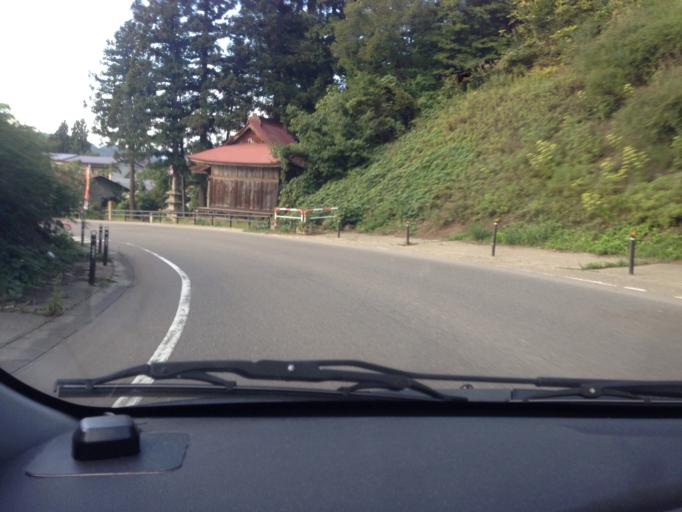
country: JP
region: Fukushima
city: Kitakata
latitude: 37.5768
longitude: 139.7696
